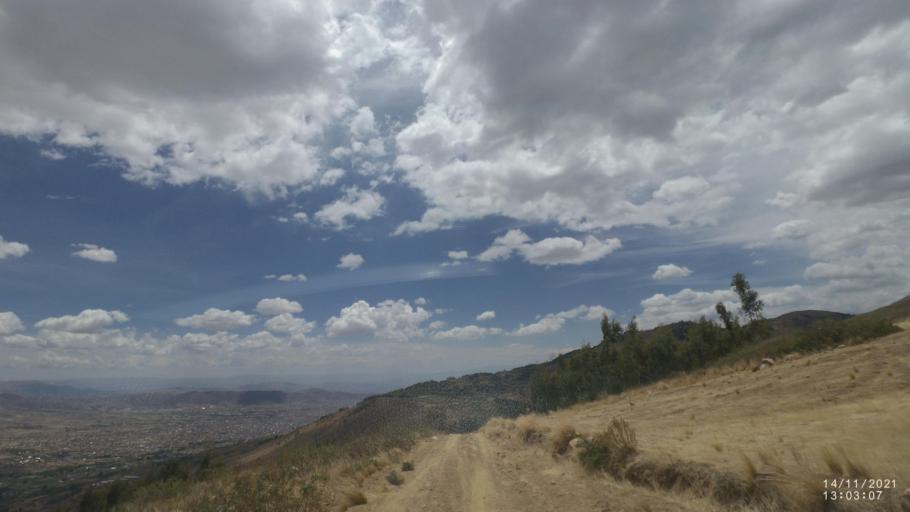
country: BO
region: Cochabamba
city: Colomi
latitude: -17.3699
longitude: -65.9760
